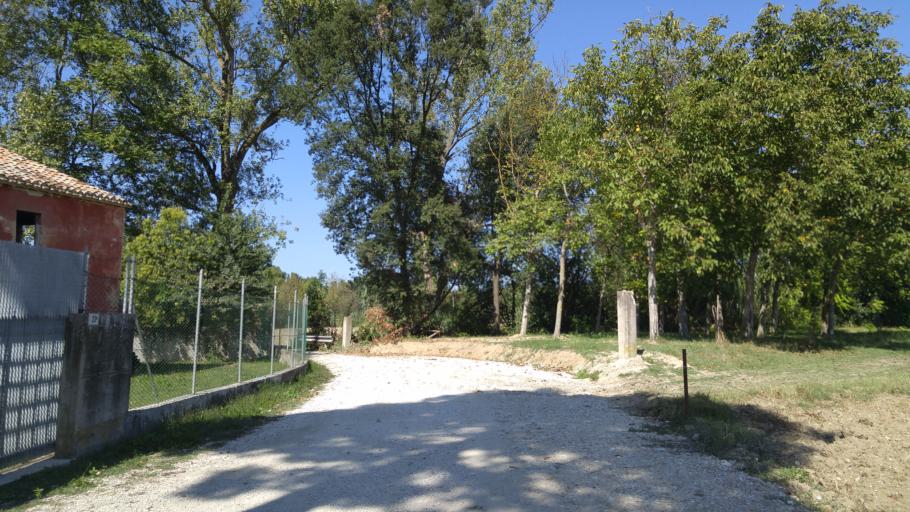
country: IT
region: The Marches
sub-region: Provincia di Pesaro e Urbino
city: Villanova
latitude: 43.7531
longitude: 12.9370
